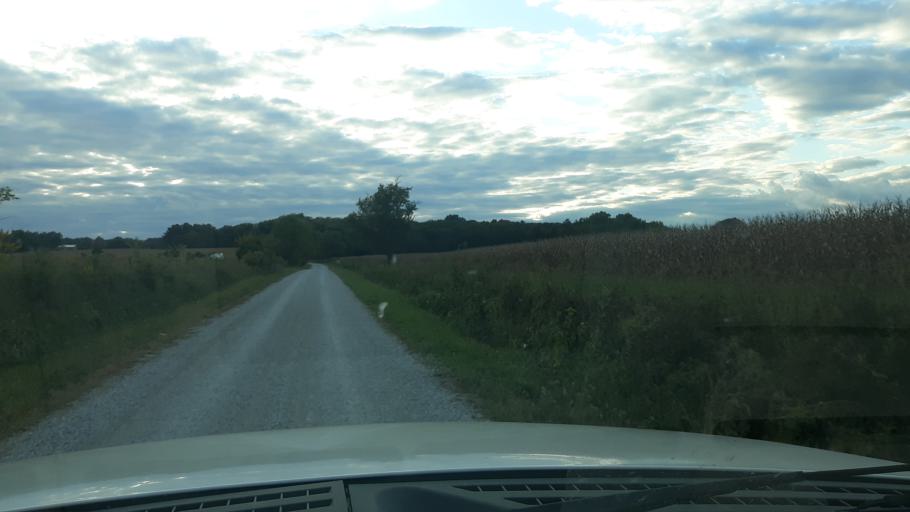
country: US
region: Illinois
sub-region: Saline County
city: Eldorado
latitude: 37.8373
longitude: -88.4757
